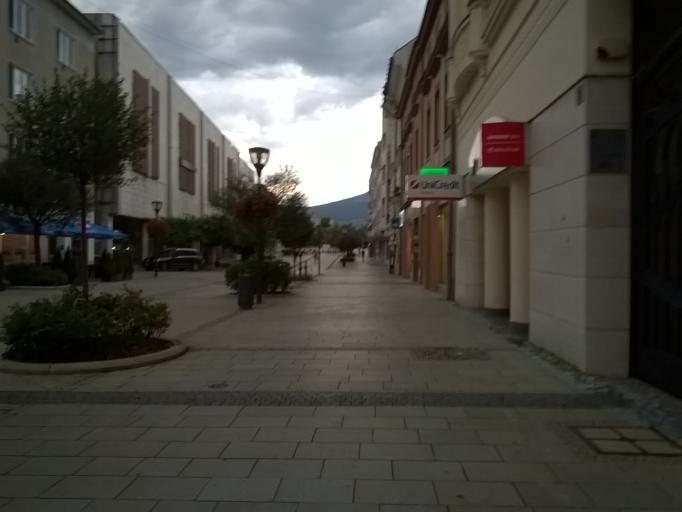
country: SK
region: Nitriansky
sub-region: Okres Nitra
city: Nitra
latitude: 48.3118
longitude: 18.0872
